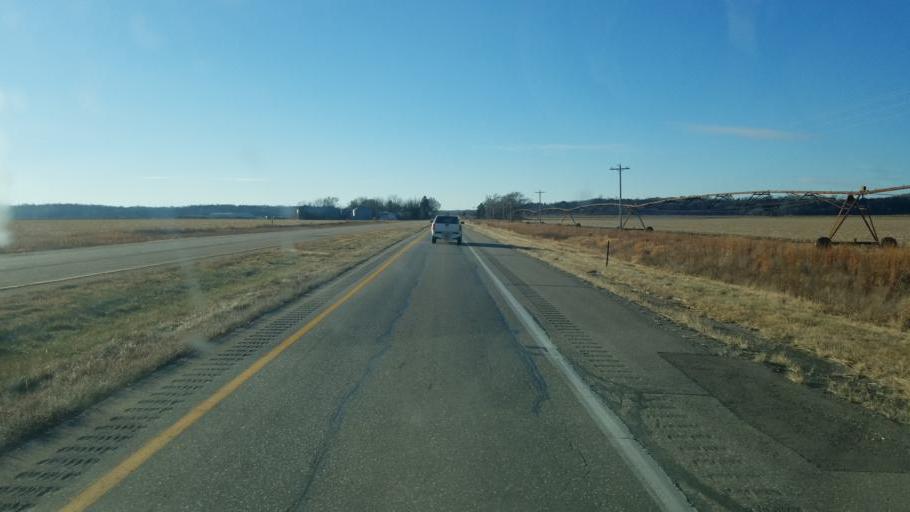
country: US
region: South Dakota
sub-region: Union County
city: Dakota Dunes
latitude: 42.4485
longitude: -96.5434
